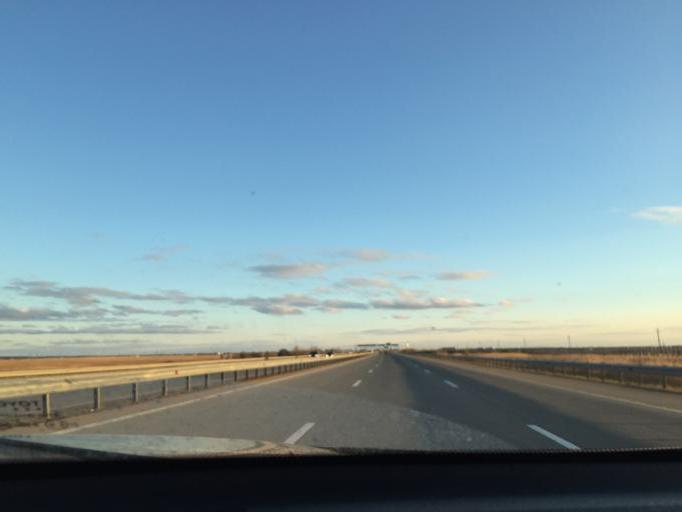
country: KZ
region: Astana Qalasy
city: Astana
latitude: 51.2778
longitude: 71.3644
